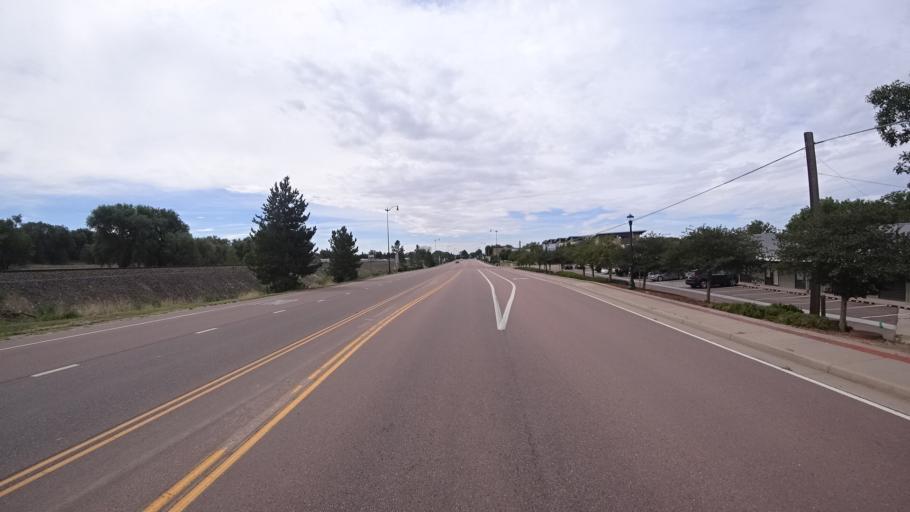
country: US
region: Colorado
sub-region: El Paso County
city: Fountain
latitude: 38.6946
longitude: -104.7051
